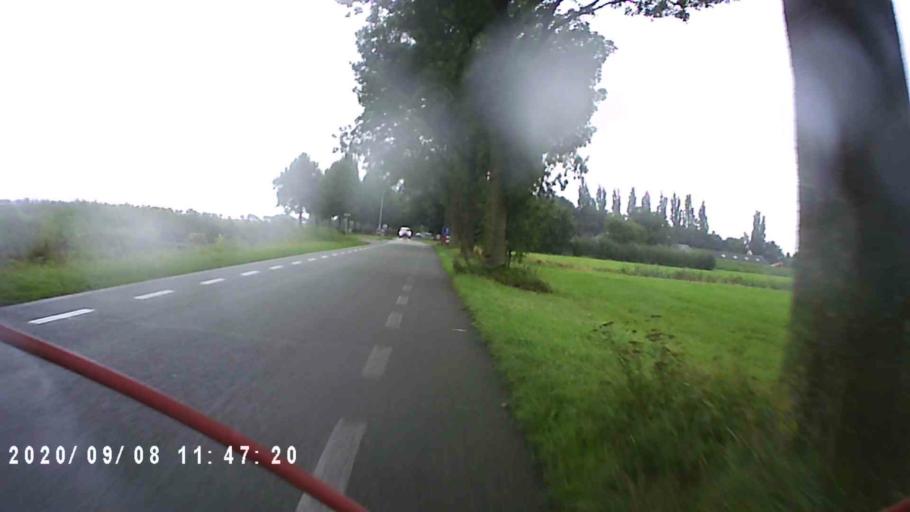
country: NL
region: Groningen
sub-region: Gemeente Hoogezand-Sappemeer
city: Sappemeer
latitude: 53.1416
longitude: 6.8009
